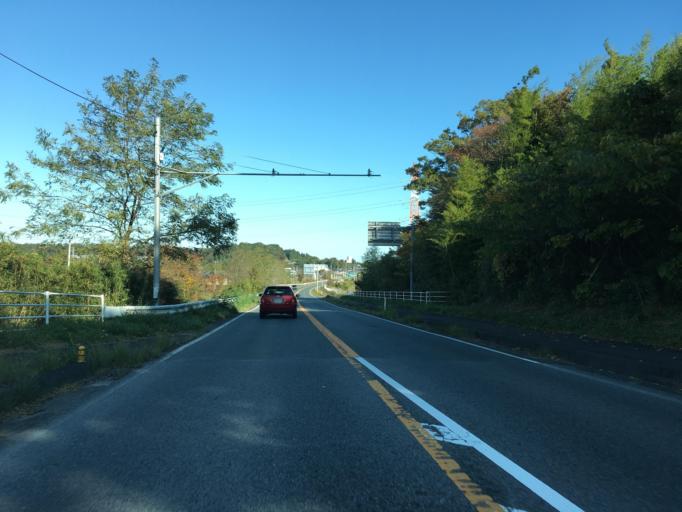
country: JP
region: Miyagi
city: Marumori
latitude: 37.8465
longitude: 140.9168
